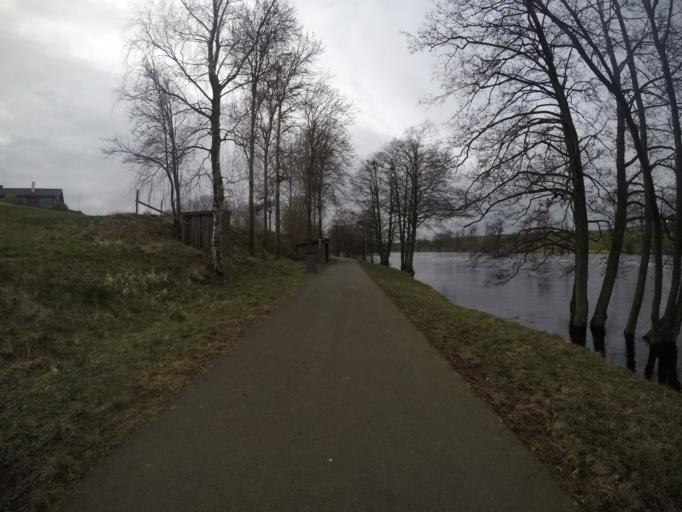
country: SE
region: Halland
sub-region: Laholms Kommun
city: Laholm
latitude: 56.5103
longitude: 13.0301
